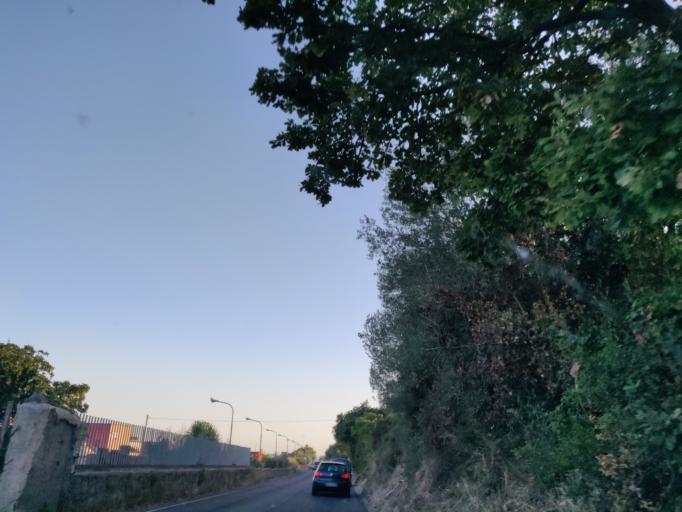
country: IT
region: Latium
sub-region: Provincia di Viterbo
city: Canino
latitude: 42.4511
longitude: 11.7366
